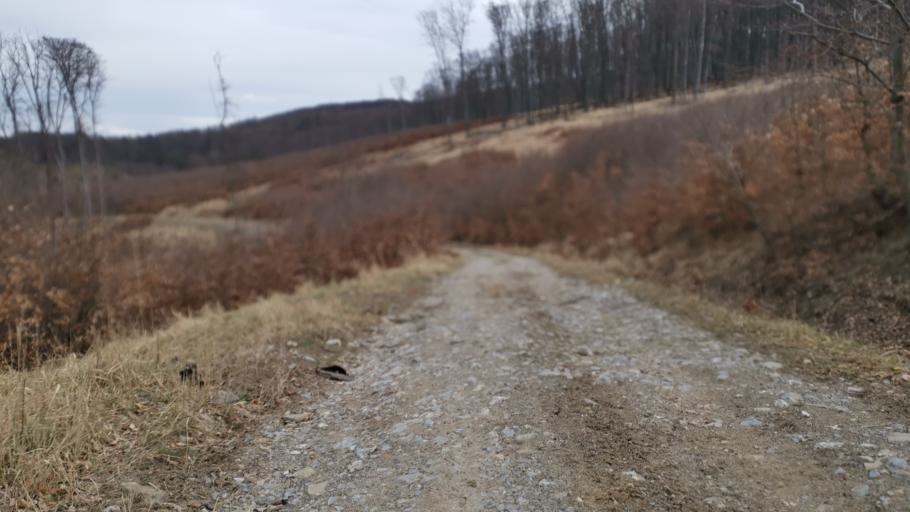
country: CZ
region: South Moravian
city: Knezdub
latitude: 48.8183
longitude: 17.3496
